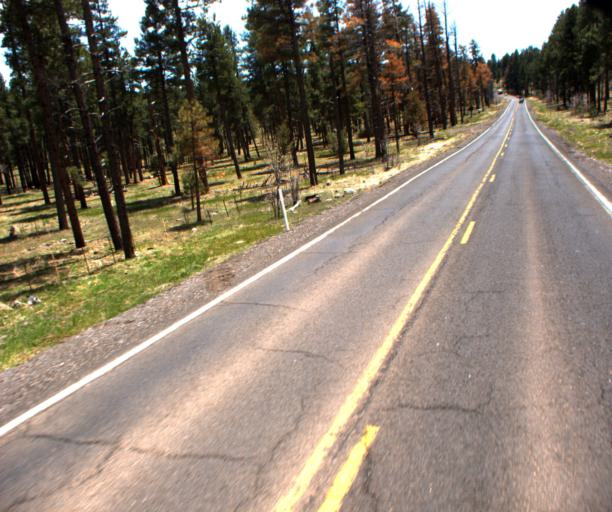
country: US
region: Arizona
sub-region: Coconino County
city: Kachina Village
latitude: 35.0449
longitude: -111.7334
